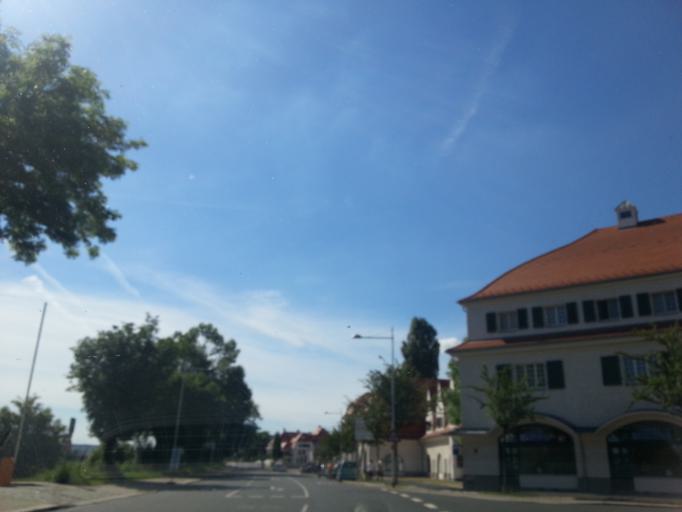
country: DE
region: Saxony
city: Dresden
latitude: 51.0678
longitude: 13.7202
